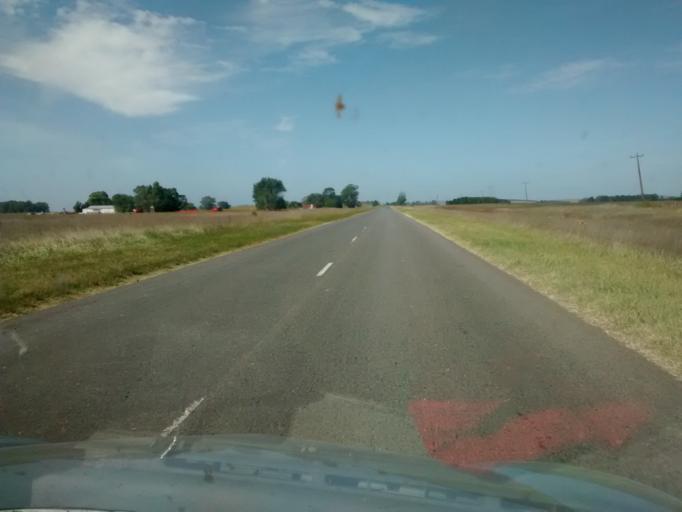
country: AR
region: Buenos Aires
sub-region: Partido de Balcarce
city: Balcarce
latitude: -37.6495
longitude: -58.4817
